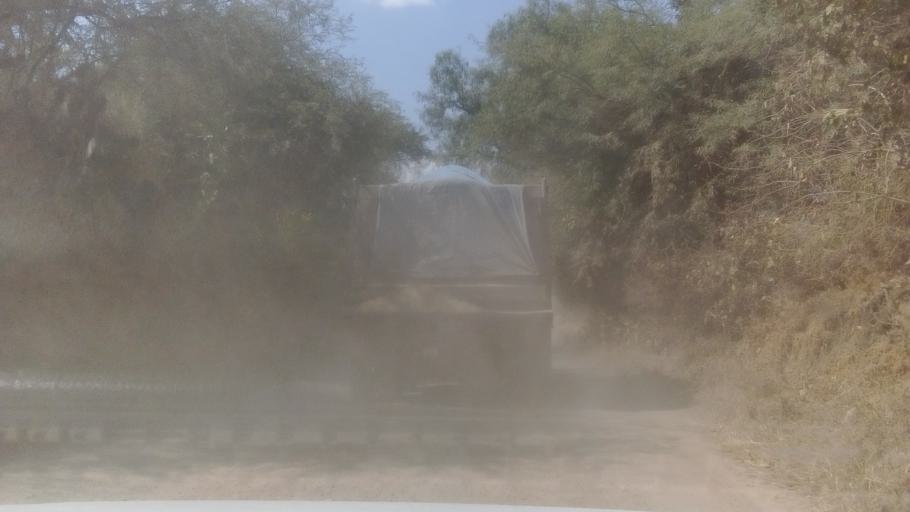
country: MX
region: Guanajuato
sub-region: Silao de la Victoria
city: San Francisco (Banos de Agua Caliente)
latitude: 21.0713
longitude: -101.4614
